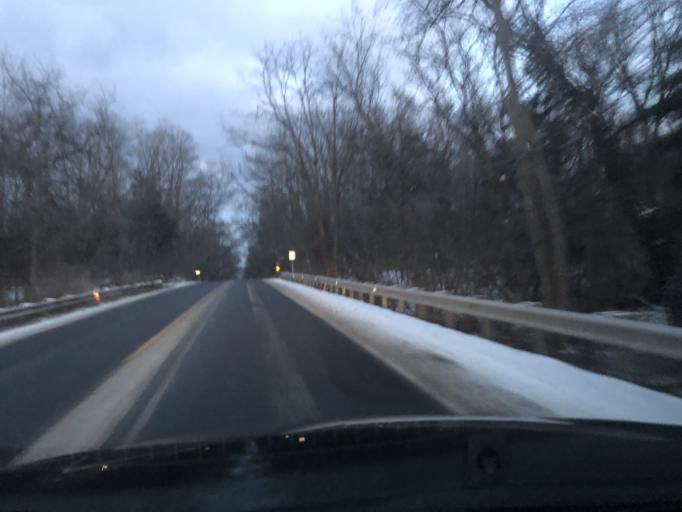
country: US
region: Michigan
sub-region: Oakland County
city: Milford
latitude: 42.5784
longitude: -83.6462
